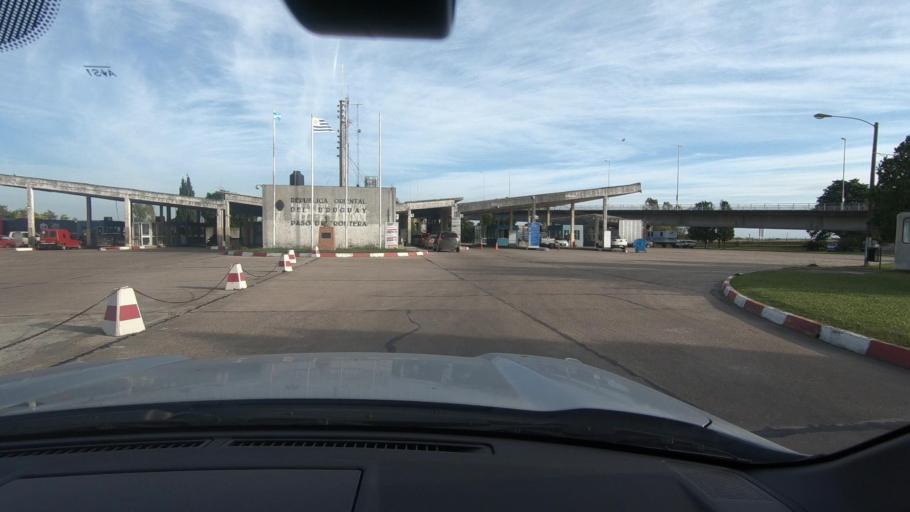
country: AR
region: Entre Rios
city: Colon
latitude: -32.2588
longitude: -58.1351
